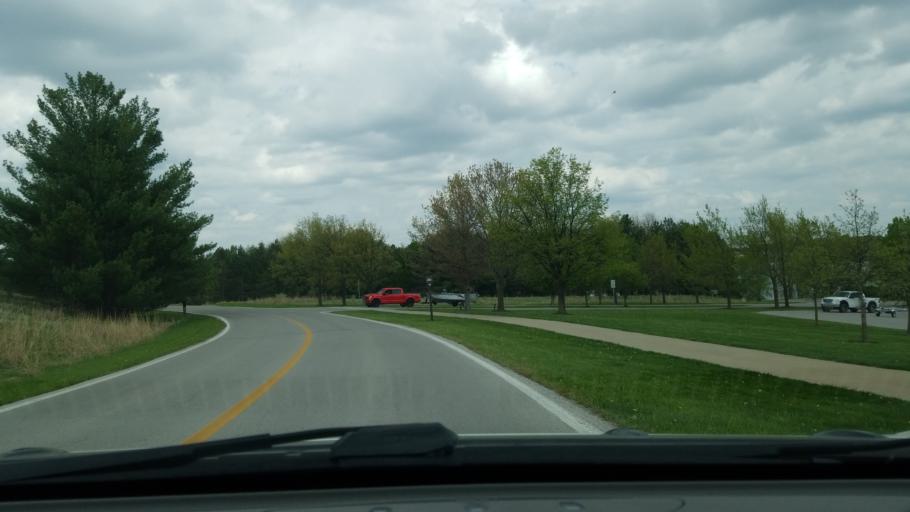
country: US
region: Nebraska
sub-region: Sarpy County
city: Chalco
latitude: 41.1653
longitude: -96.1573
